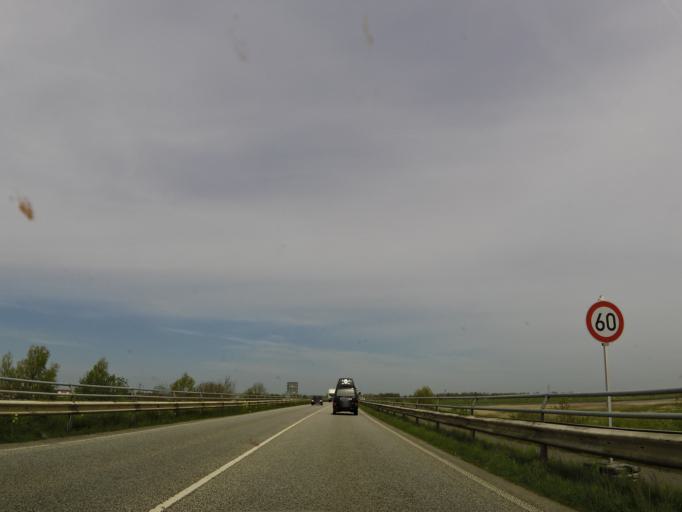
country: DE
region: Schleswig-Holstein
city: Tonning
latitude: 54.3106
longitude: 8.9578
